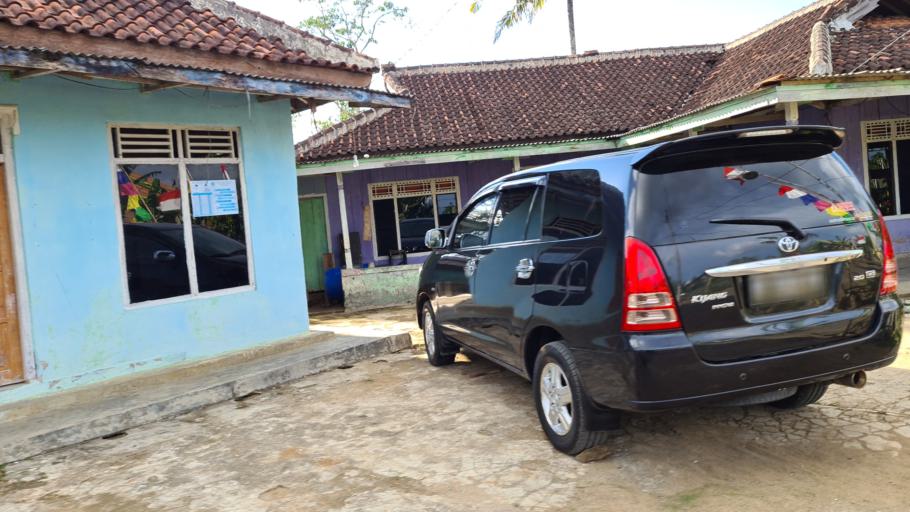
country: ID
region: Lampung
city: Kenali
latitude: -5.0929
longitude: 104.4004
